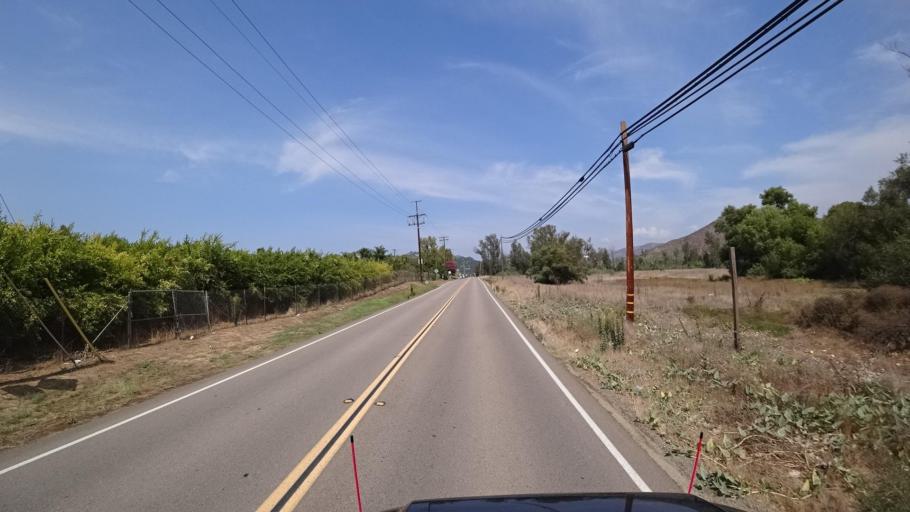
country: US
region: California
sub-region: San Diego County
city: San Pasqual
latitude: 33.0912
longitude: -117.0205
